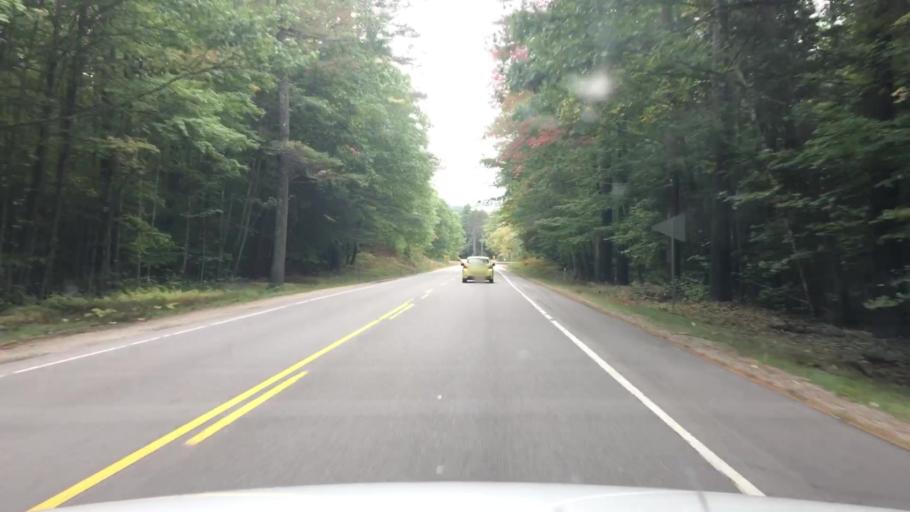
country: US
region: New Hampshire
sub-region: Carroll County
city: Tamworth
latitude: 43.9011
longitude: -71.2312
